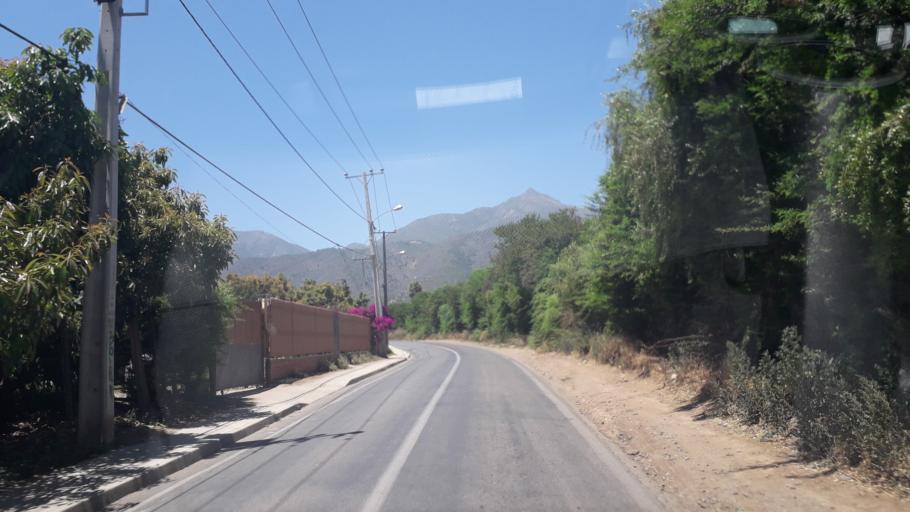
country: CL
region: Valparaiso
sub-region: Provincia de Quillota
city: Quillota
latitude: -32.9076
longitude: -71.2164
